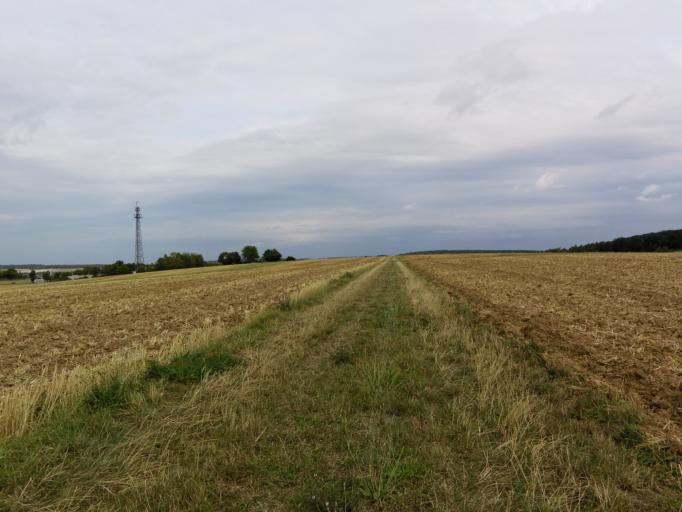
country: DE
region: Bavaria
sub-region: Regierungsbezirk Unterfranken
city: Rimpar
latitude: 49.8383
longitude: 9.9388
